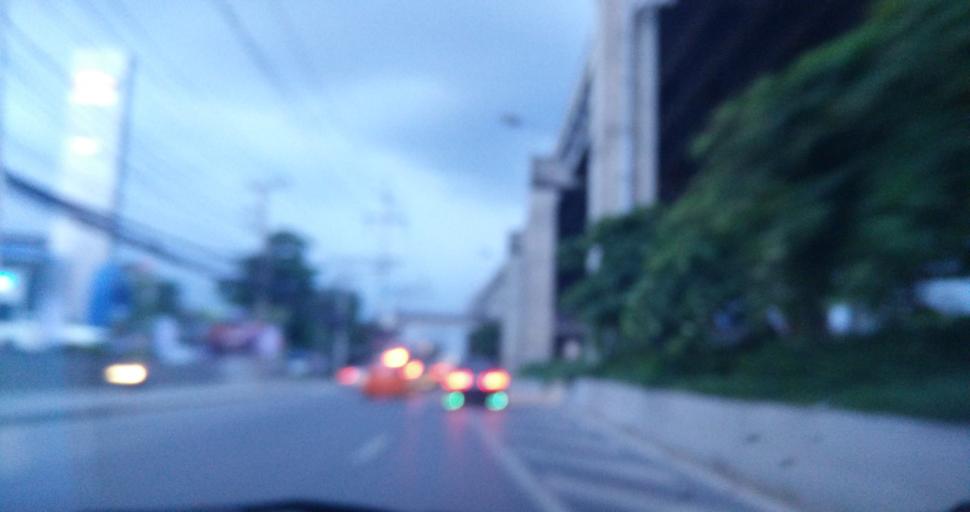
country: TH
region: Phra Nakhon Si Ayutthaya
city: Ban Bang Kadi Pathum Thani
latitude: 13.9995
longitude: 100.6147
